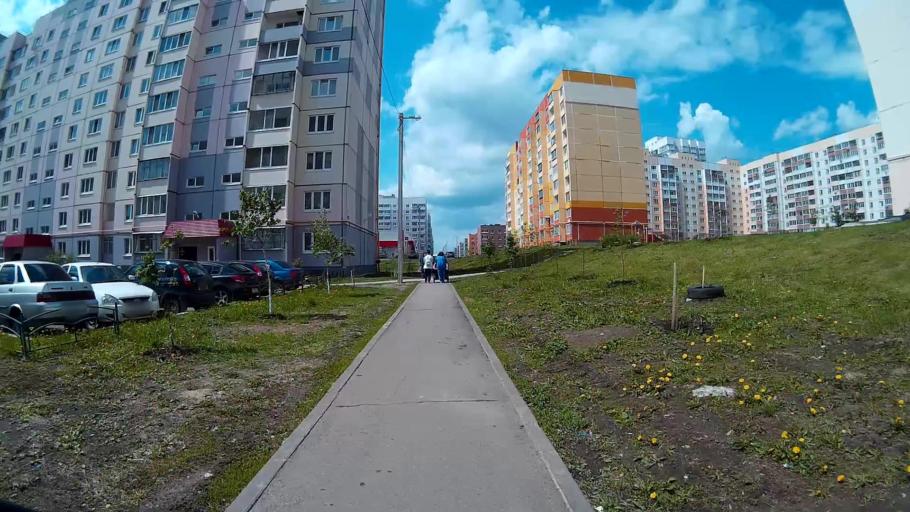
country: RU
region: Ulyanovsk
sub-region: Ulyanovskiy Rayon
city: Ulyanovsk
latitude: 54.3481
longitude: 48.3448
